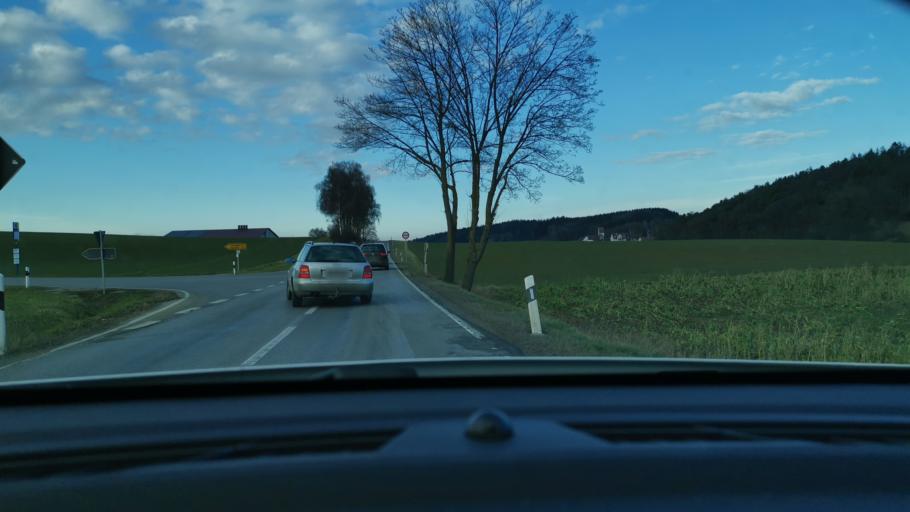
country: DE
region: Bavaria
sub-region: Swabia
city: Aindling
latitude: 48.5603
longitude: 10.9844
